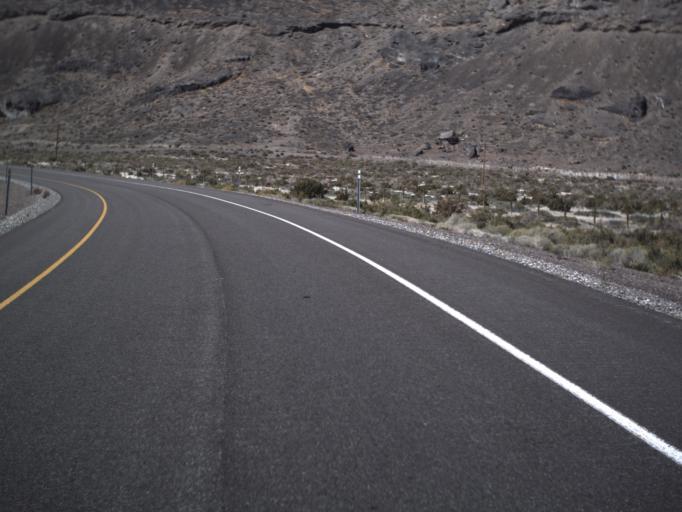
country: US
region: Utah
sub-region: Tooele County
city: Wendover
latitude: 40.7494
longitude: -114.0120
